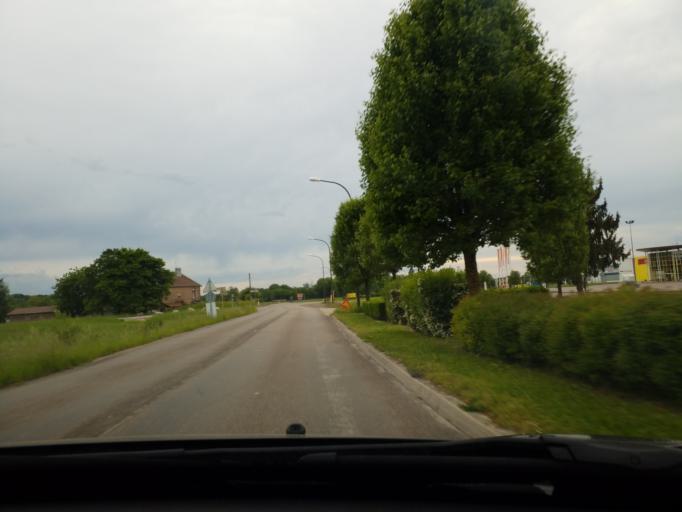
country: FR
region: Franche-Comte
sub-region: Departement de la Haute-Saone
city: Saint-Loup-sur-Semouse
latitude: 47.8809
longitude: 6.3040
